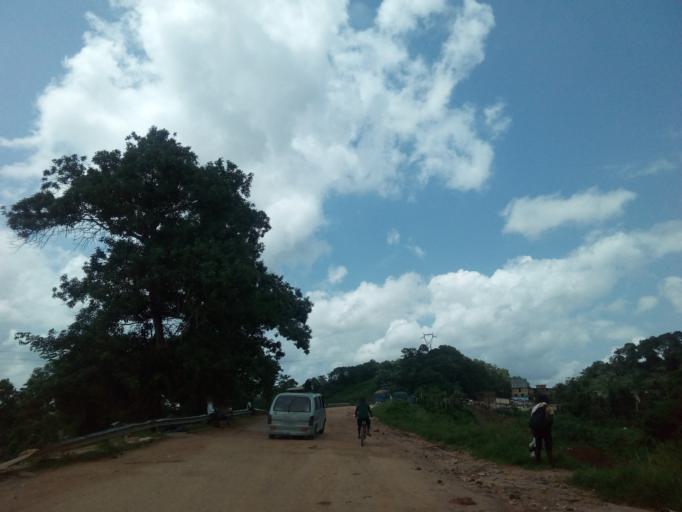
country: CI
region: Sud-Comoe
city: Mafere
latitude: 5.2904
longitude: -2.7930
